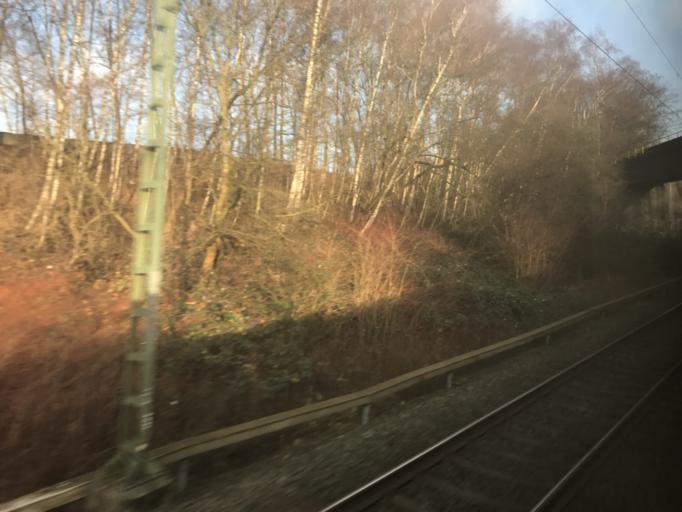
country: DE
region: North Rhine-Westphalia
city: Witten
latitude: 51.4845
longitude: 7.3388
